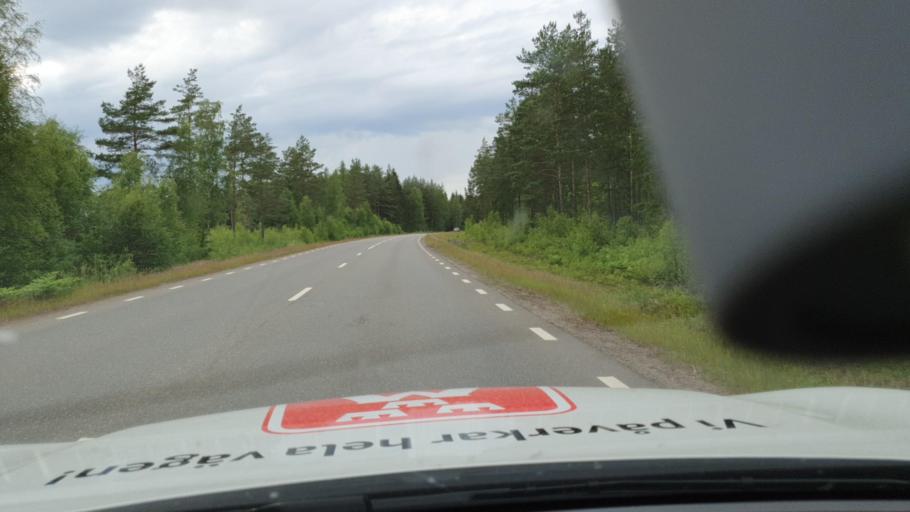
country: SE
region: Vaestra Goetaland
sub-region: Karlsborgs Kommun
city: Karlsborg
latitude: 58.5783
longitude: 14.4582
